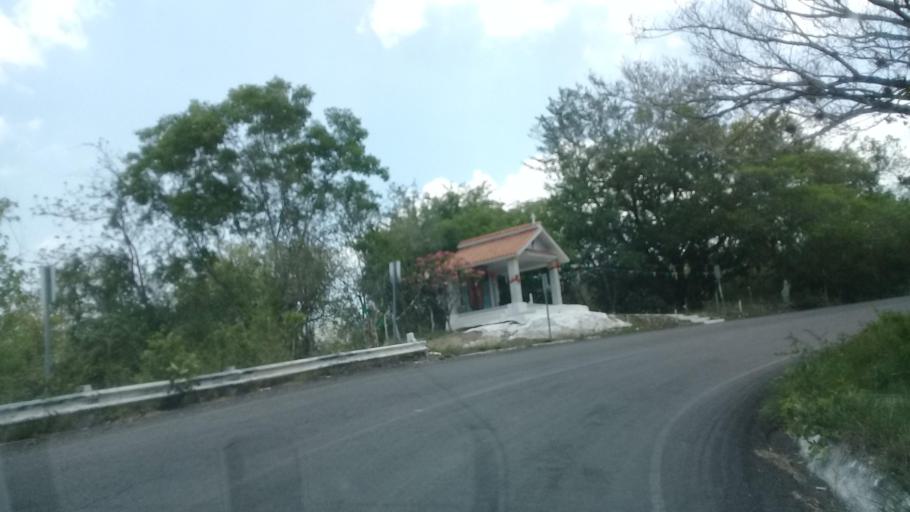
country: MX
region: Veracruz
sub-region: Emiliano Zapata
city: Plan del Rio
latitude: 19.4168
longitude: -96.6124
